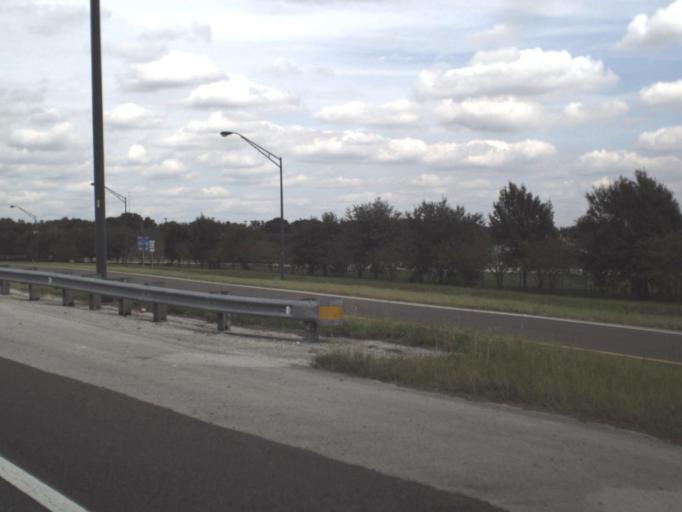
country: US
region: Florida
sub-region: Polk County
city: Winston
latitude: 28.0262
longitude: -82.0400
